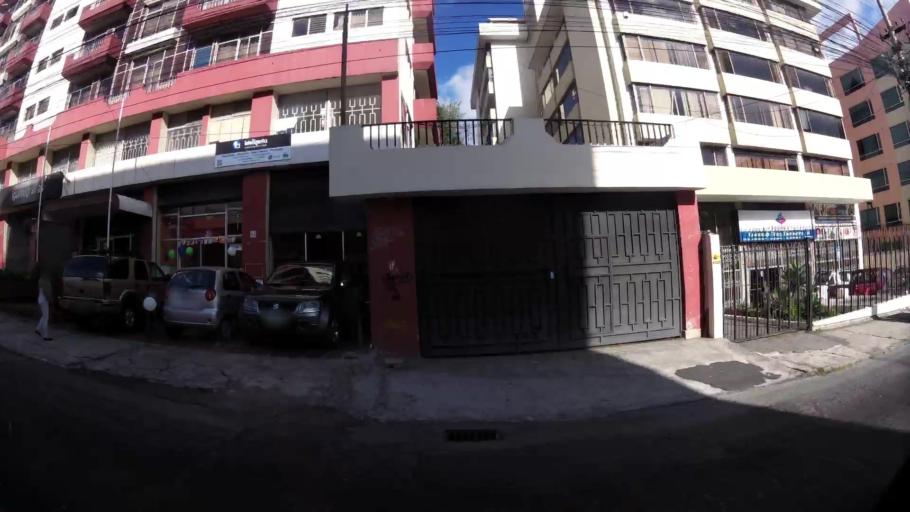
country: EC
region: Pichincha
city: Quito
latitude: -0.2088
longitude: -78.4859
